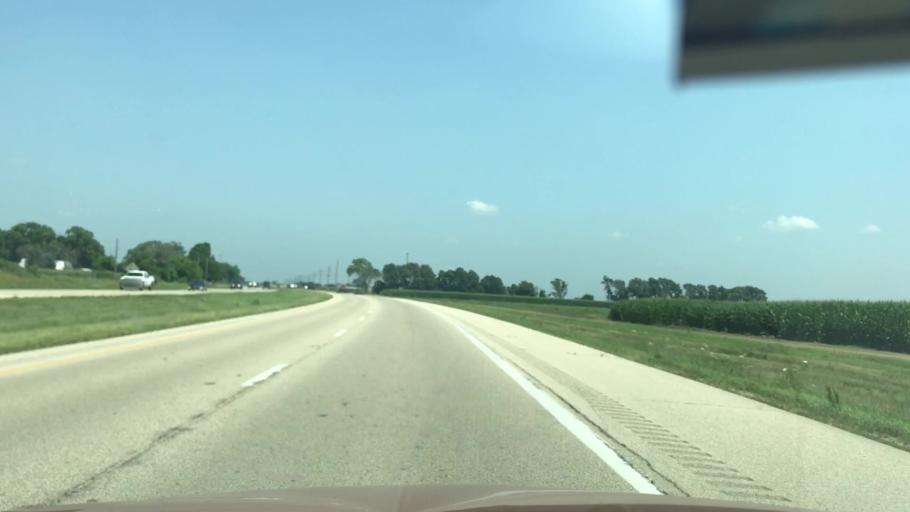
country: US
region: Illinois
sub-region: Winnebago County
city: Cherry Valley
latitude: 42.2376
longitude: -88.9356
